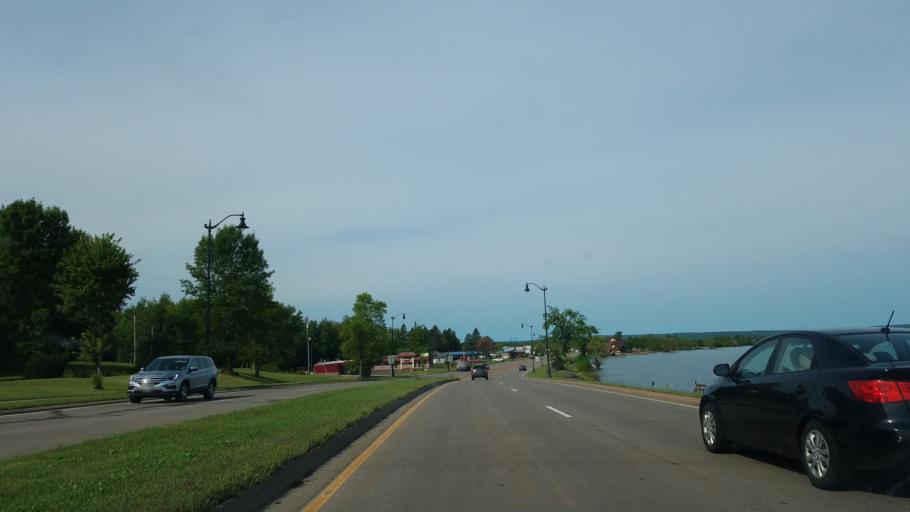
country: US
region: Wisconsin
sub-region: Ashland County
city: Ashland
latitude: 46.5826
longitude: -90.9085
